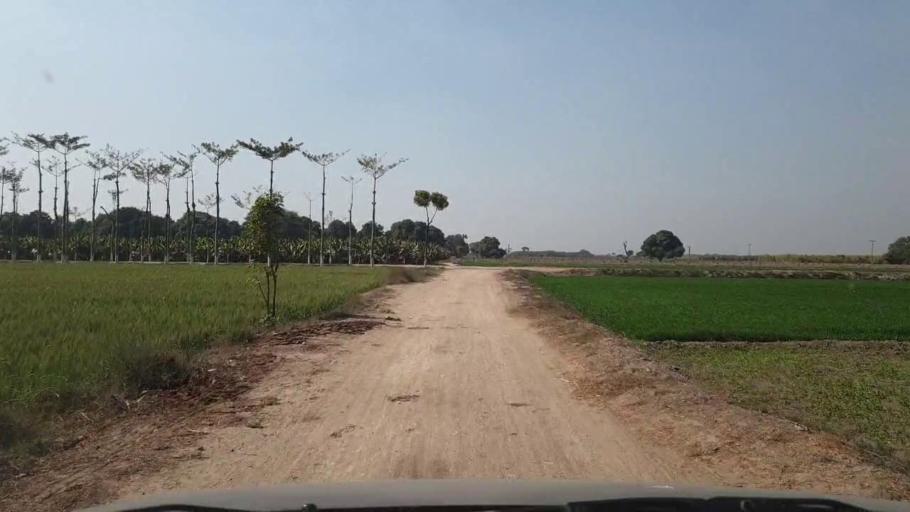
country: PK
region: Sindh
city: Tando Jam
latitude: 25.4034
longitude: 68.6287
